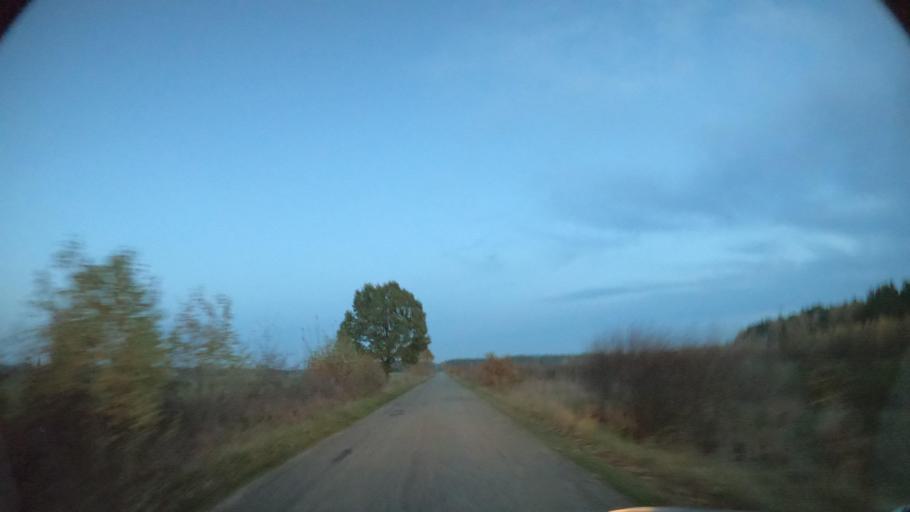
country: PL
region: Greater Poland Voivodeship
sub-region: Powiat zlotowski
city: Sypniewo
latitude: 53.4265
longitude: 16.6598
